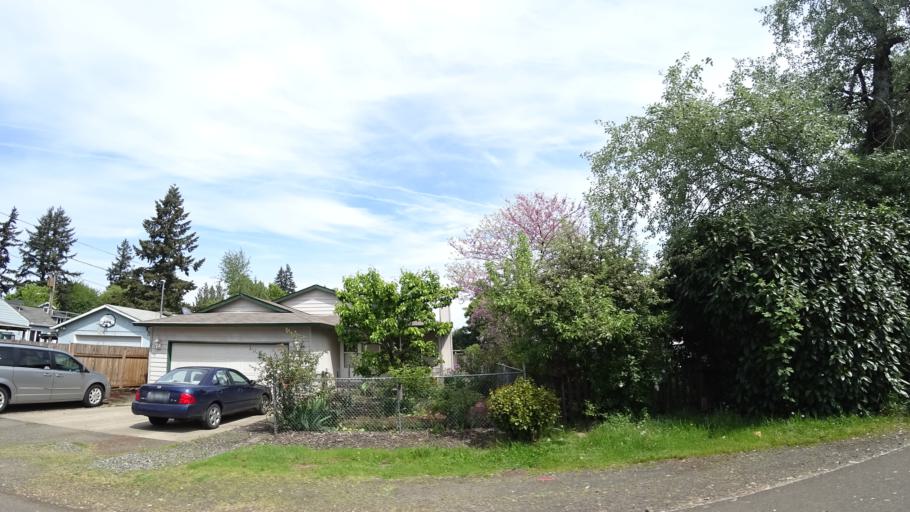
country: US
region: Oregon
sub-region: Multnomah County
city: Lents
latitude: 45.4668
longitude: -122.6022
